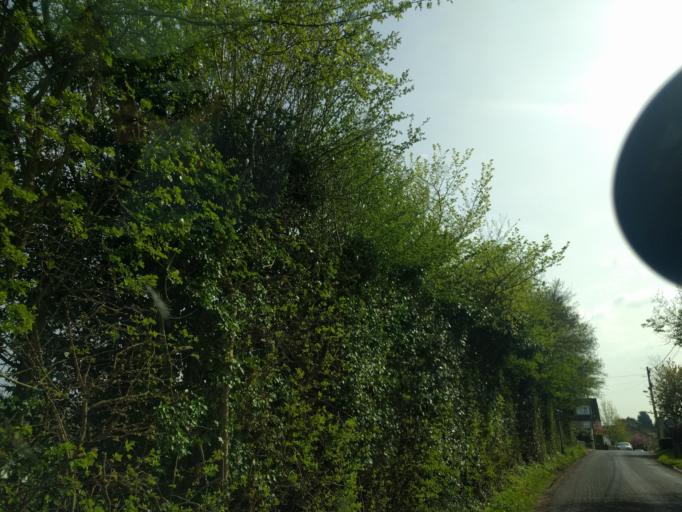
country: GB
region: England
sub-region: Wiltshire
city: Corsham
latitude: 51.4181
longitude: -2.1656
